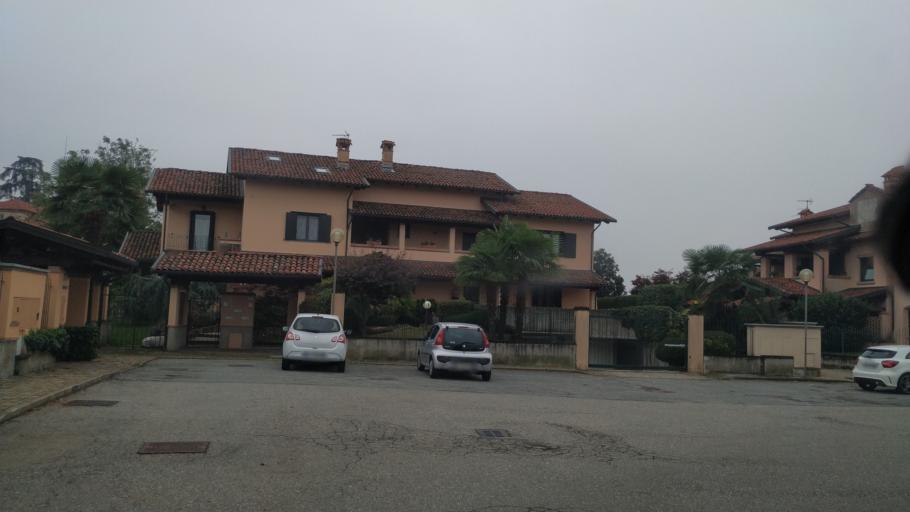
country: IT
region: Piedmont
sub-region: Provincia di Biella
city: Lessona
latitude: 45.5849
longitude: 8.1953
